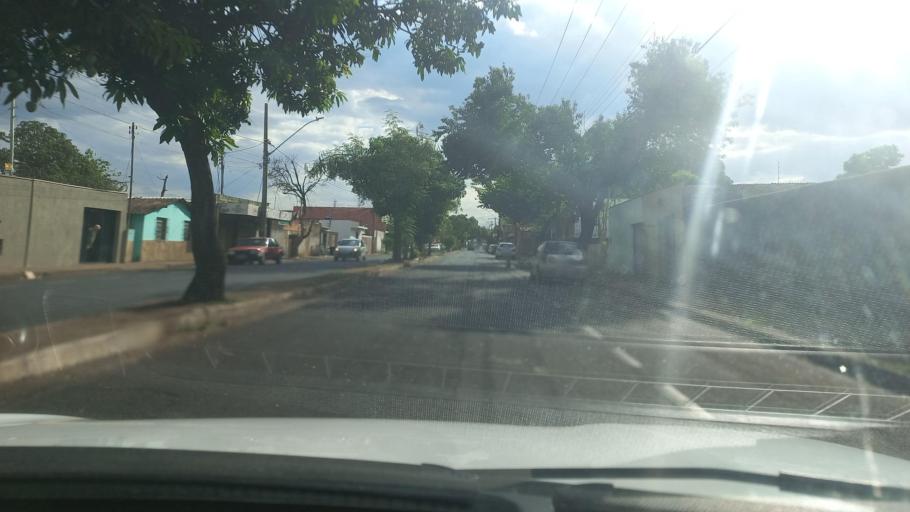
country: BR
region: Minas Gerais
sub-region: Uberaba
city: Uberaba
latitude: -19.7606
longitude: -47.9121
